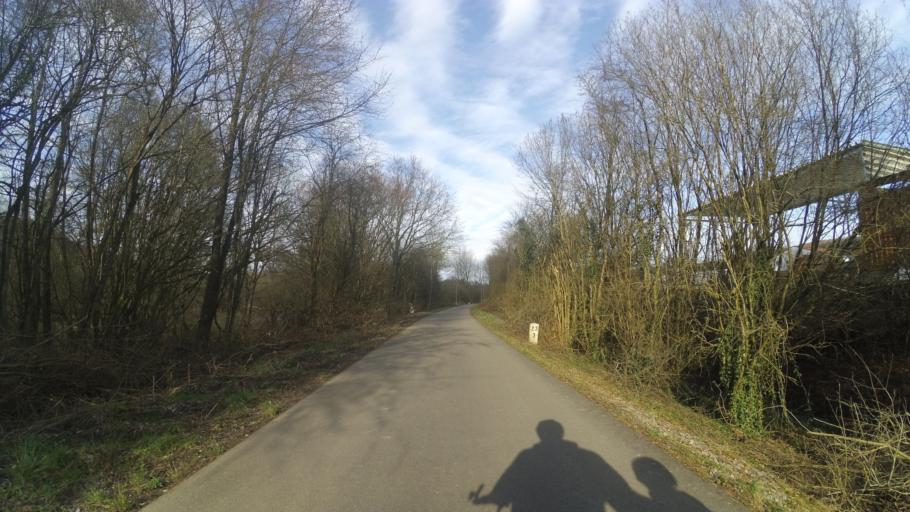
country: DE
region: Saarland
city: Gersheim
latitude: 49.1581
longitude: 7.2093
